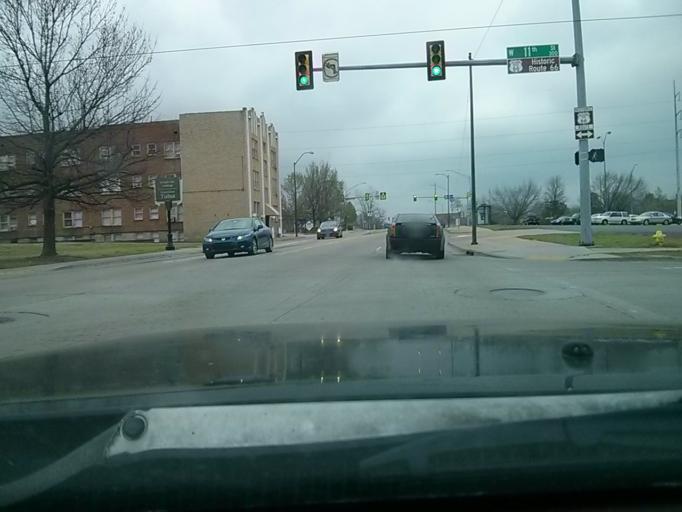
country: US
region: Oklahoma
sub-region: Tulsa County
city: Tulsa
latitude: 36.1460
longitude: -95.9924
